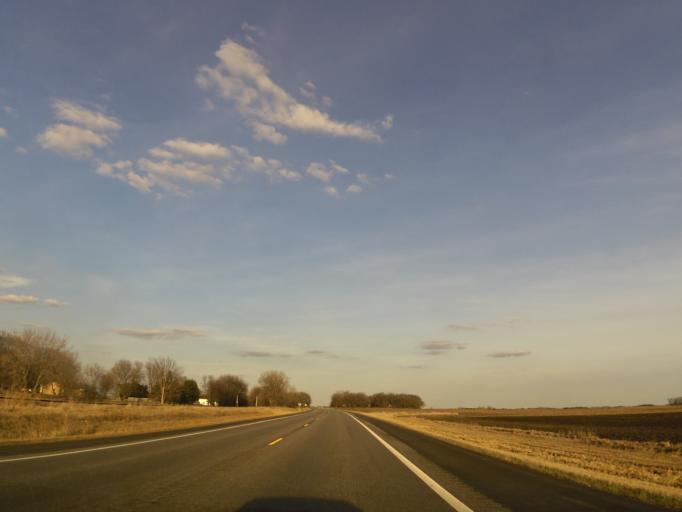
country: US
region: Minnesota
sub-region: McLeod County
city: Glencoe
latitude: 44.7393
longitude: -94.2662
